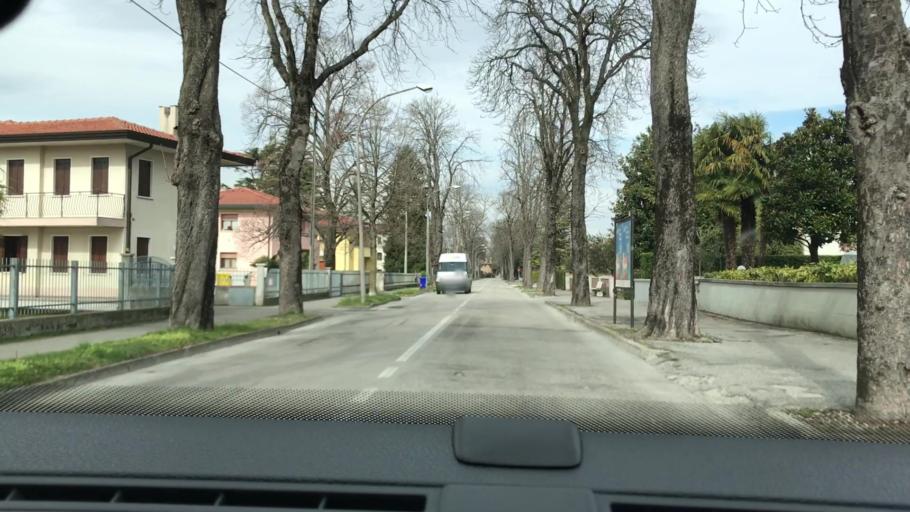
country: IT
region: Veneto
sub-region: Provincia di Venezia
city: Santo Stino di Livenza
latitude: 45.7228
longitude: 12.6810
